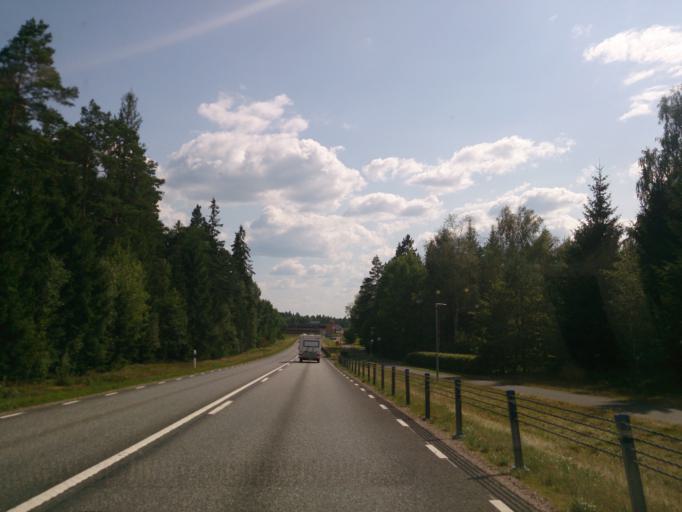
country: SE
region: Joenkoeping
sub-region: Gislaveds Kommun
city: Smalandsstenar
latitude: 57.1298
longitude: 13.3795
